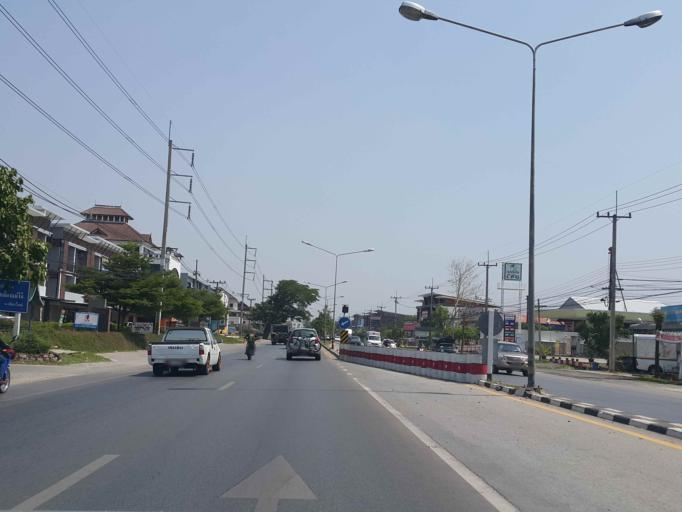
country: TH
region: Chiang Mai
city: San Sai
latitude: 18.8702
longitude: 99.0154
